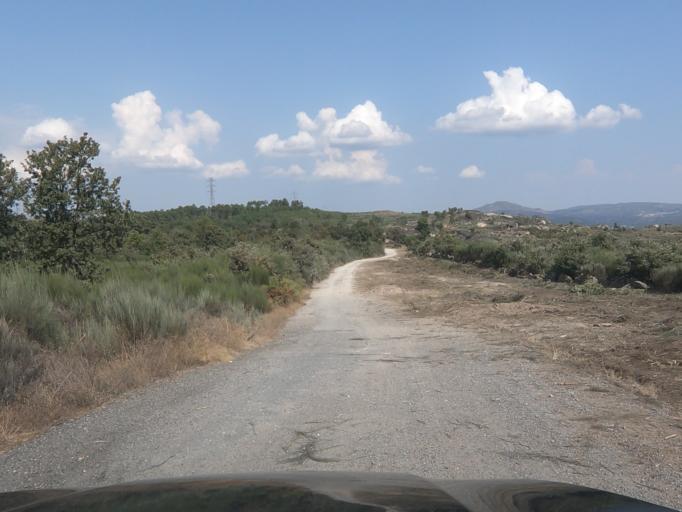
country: PT
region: Vila Real
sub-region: Sabrosa
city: Sabrosa
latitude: 41.3153
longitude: -7.6214
